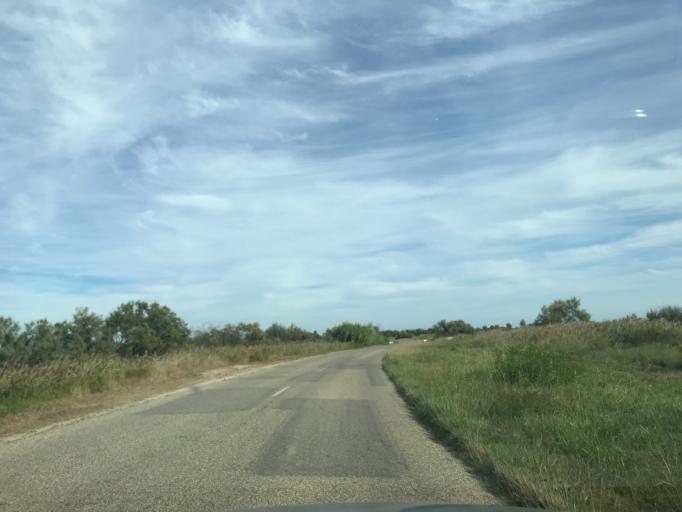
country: FR
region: Provence-Alpes-Cote d'Azur
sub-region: Departement des Bouches-du-Rhone
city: Saintes-Maries-de-la-Mer
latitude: 43.5210
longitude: 4.3902
